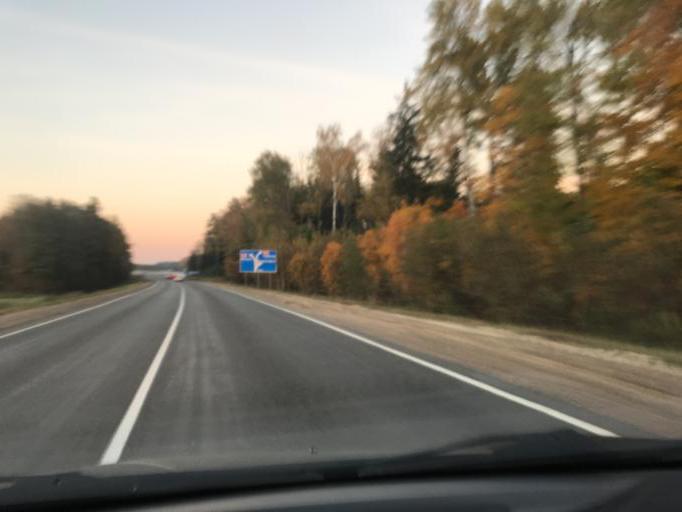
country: BY
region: Mogilev
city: Babruysk
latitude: 53.2021
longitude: 29.0681
